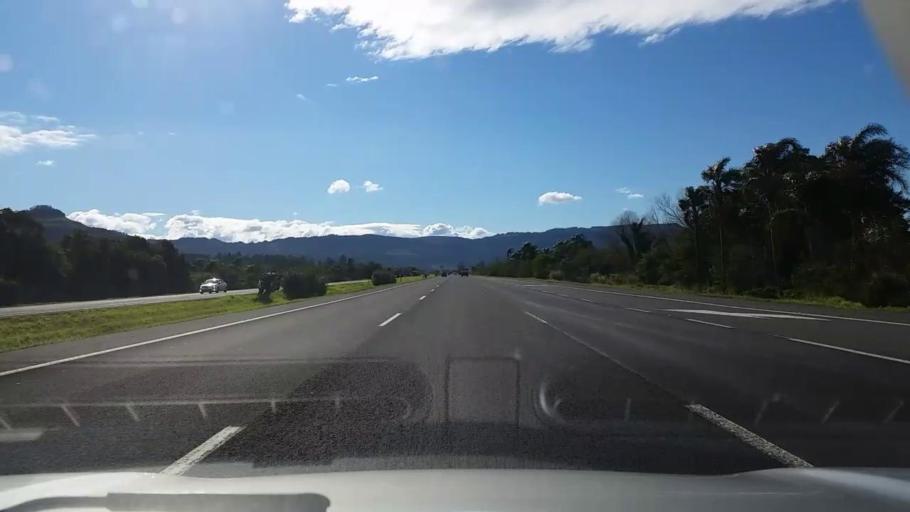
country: BR
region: Rio Grande do Sul
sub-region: Osorio
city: Osorio
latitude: -29.8842
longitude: -50.4435
